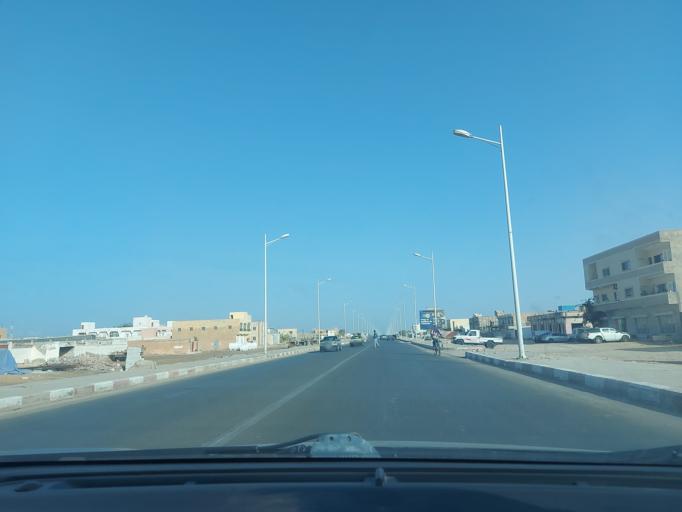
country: MR
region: Nouakchott
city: Nouakchott
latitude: 18.0870
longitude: -16.0036
